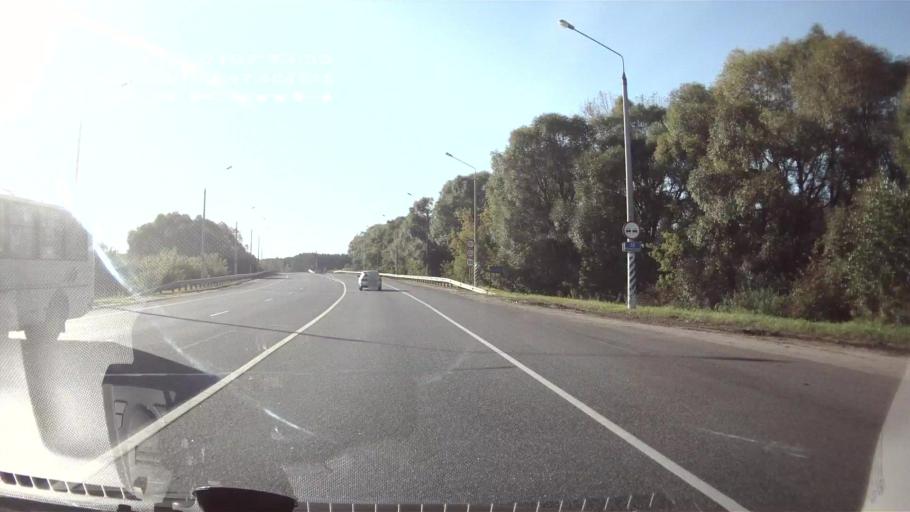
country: RU
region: Chuvashia
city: Shikhazany
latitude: 55.5598
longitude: 47.4051
